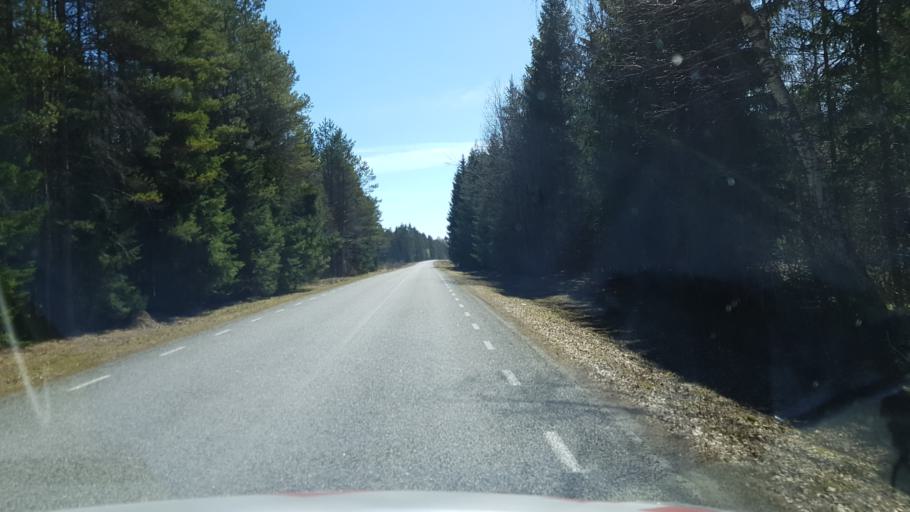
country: EE
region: Laeaene-Virumaa
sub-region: Vinni vald
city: Vinni
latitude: 59.1770
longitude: 26.5032
